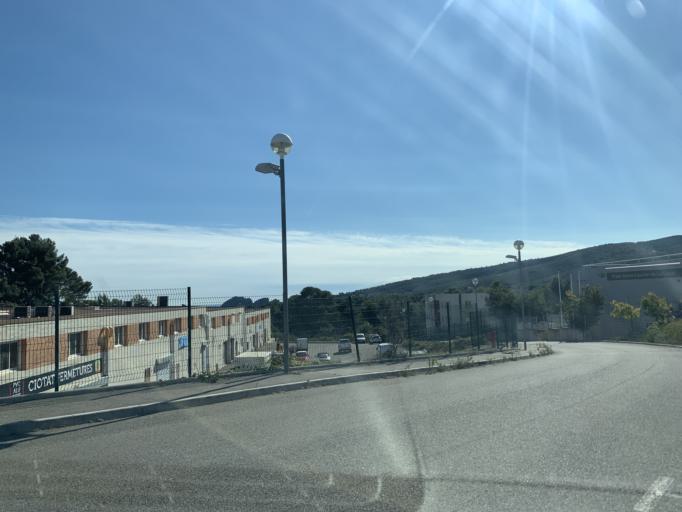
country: FR
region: Provence-Alpes-Cote d'Azur
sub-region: Departement des Bouches-du-Rhone
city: La Ciotat
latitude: 43.2021
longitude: 5.5913
